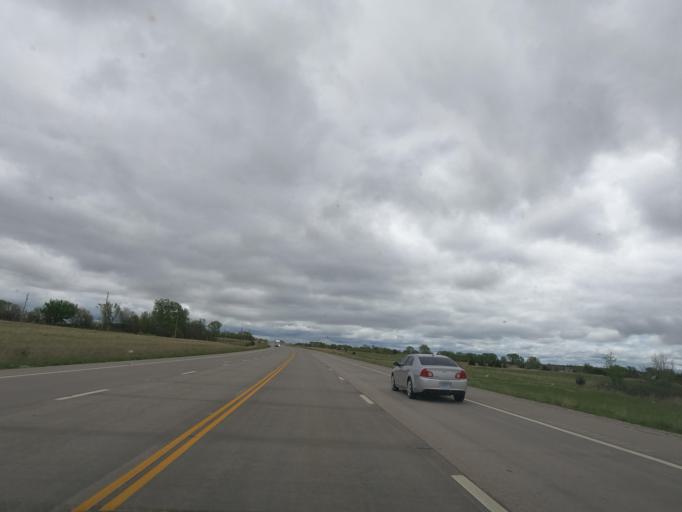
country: US
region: Kansas
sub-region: Elk County
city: Howard
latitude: 37.6348
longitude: -96.1847
